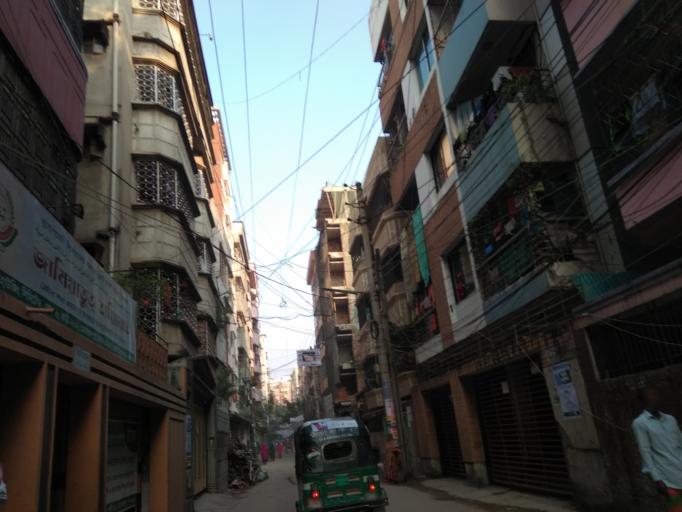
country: BD
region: Dhaka
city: Azimpur
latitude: 23.7595
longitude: 90.3552
